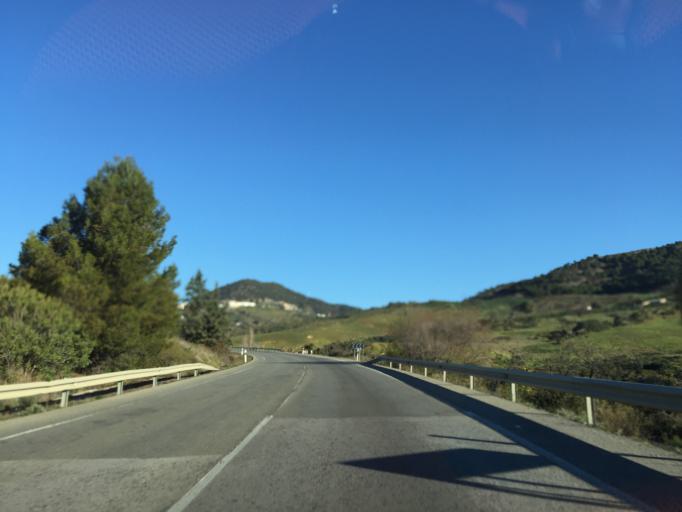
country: ES
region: Andalusia
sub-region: Provincia de Malaga
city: Carratraca
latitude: 36.8377
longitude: -4.8082
